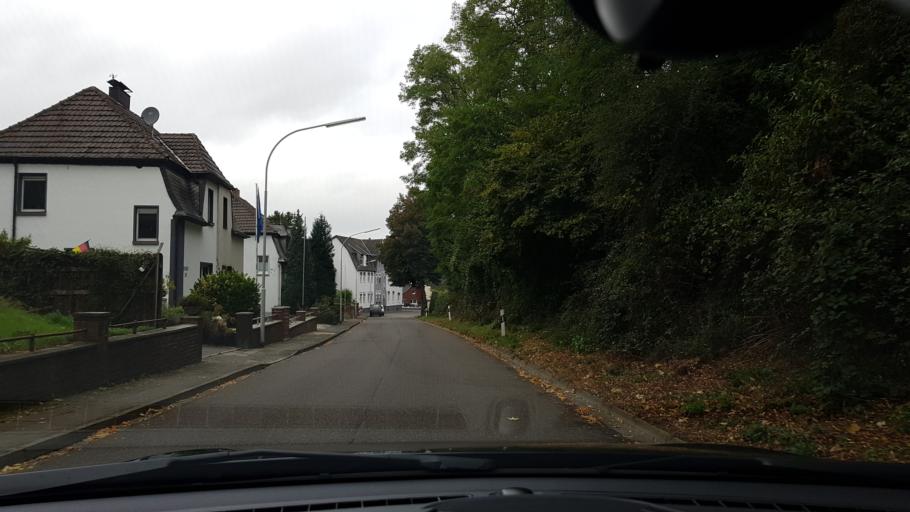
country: DE
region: North Rhine-Westphalia
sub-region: Regierungsbezirk Koln
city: Bedburg
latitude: 51.0348
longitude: 6.6010
